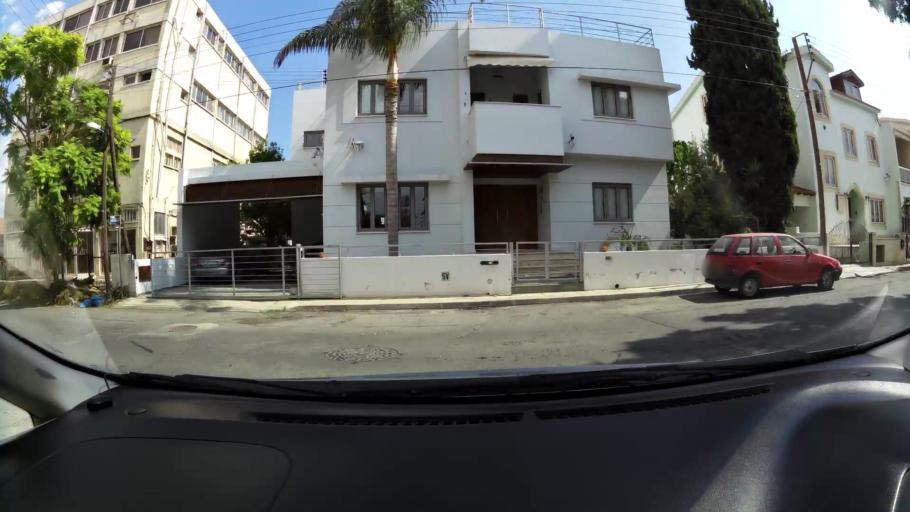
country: CY
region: Larnaka
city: Larnaca
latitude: 34.9135
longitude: 33.6184
